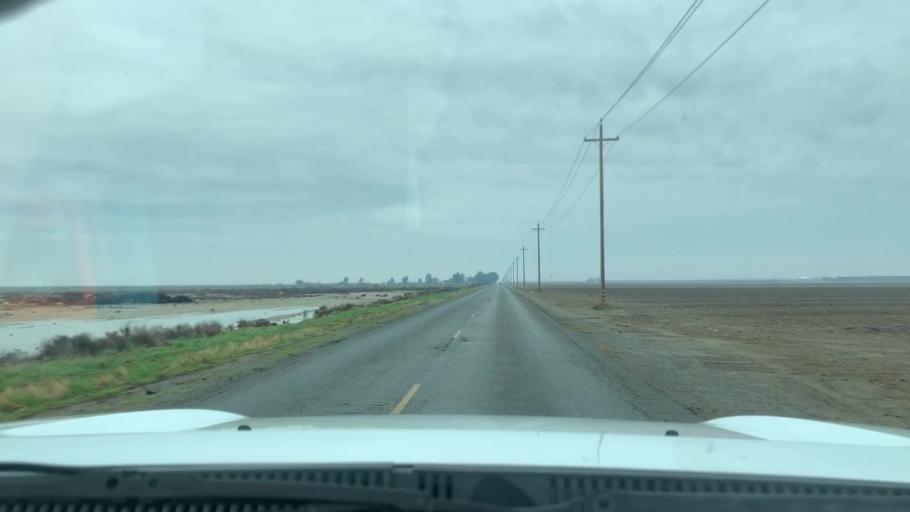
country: US
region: California
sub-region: Tulare County
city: Alpaugh
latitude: 35.7610
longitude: -119.4305
